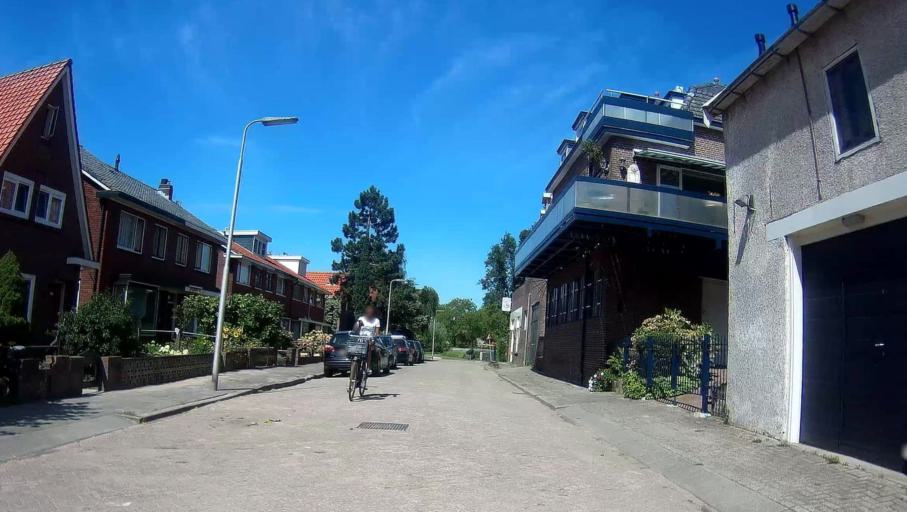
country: NL
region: South Holland
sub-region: Gemeente Ridderkerk
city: Ridderkerk
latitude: 51.8738
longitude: 4.6025
